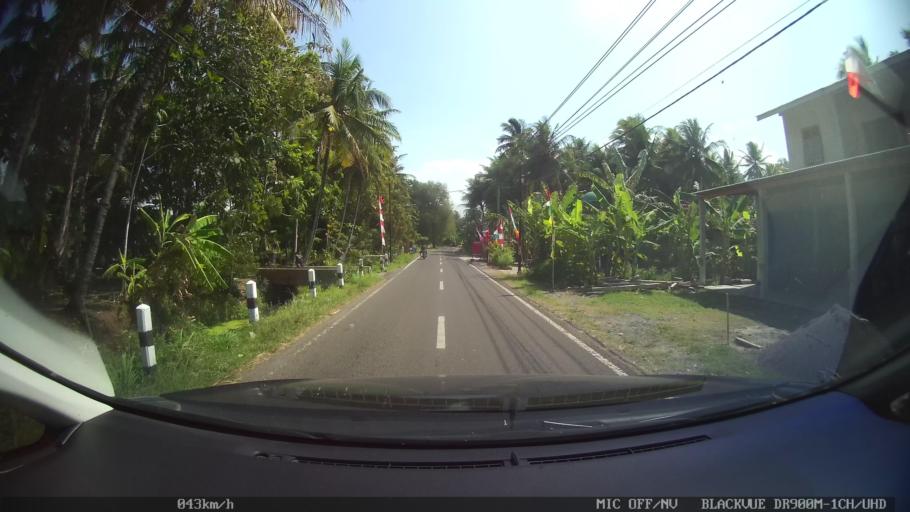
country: ID
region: Daerah Istimewa Yogyakarta
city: Srandakan
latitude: -7.9225
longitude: 110.1574
